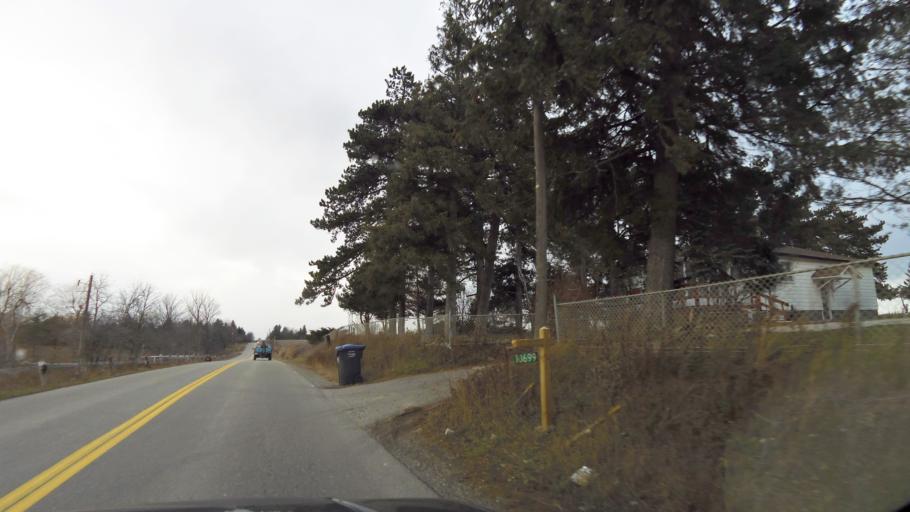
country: CA
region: Ontario
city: Brampton
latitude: 43.8149
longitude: -79.6972
